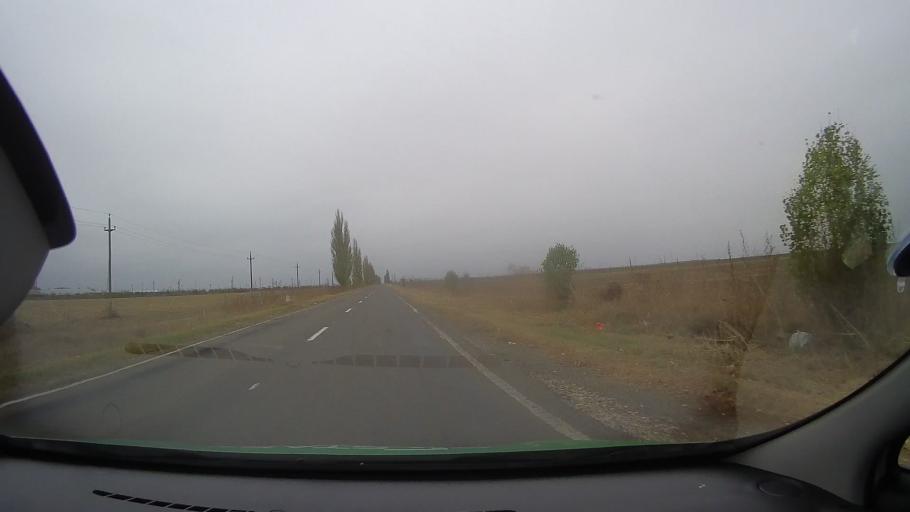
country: RO
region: Ialomita
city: Tandarei
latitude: 44.6571
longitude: 27.6503
